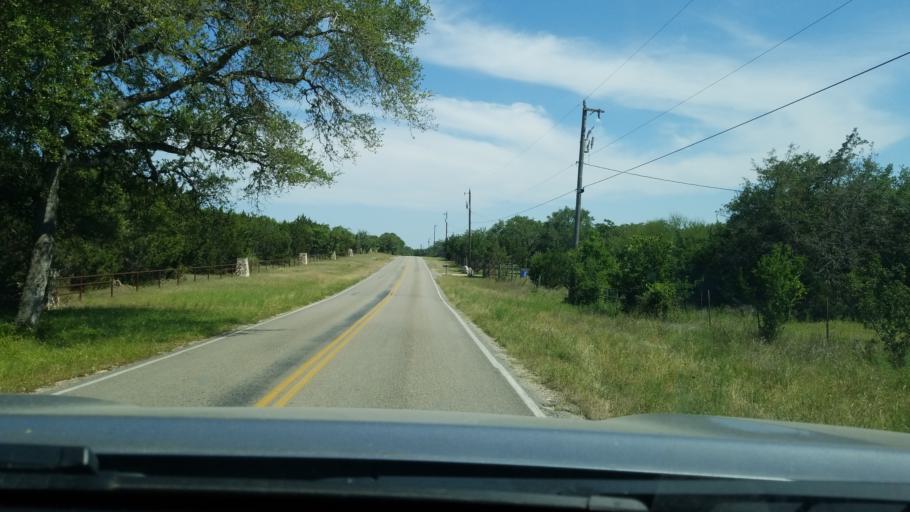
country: US
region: Texas
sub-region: Comal County
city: Bulverde
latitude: 29.7645
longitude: -98.5110
